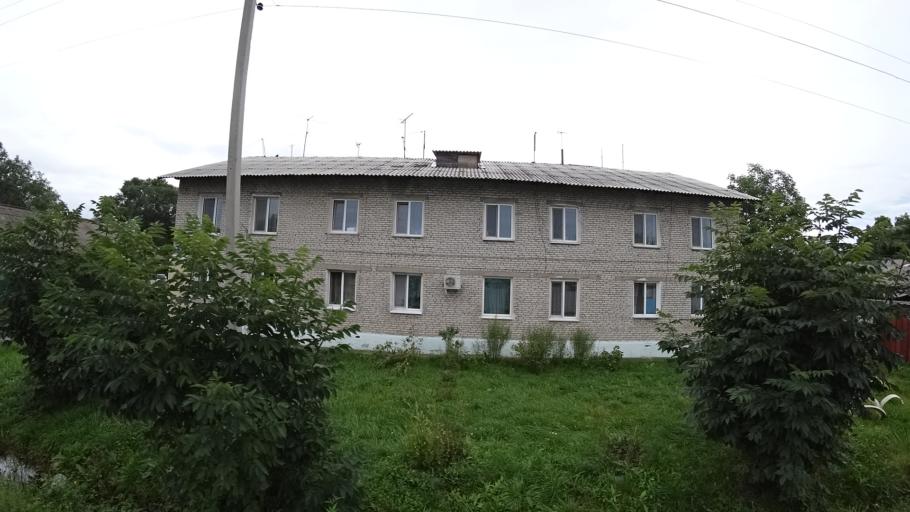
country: RU
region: Primorskiy
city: Chernigovka
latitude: 44.3405
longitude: 132.5767
